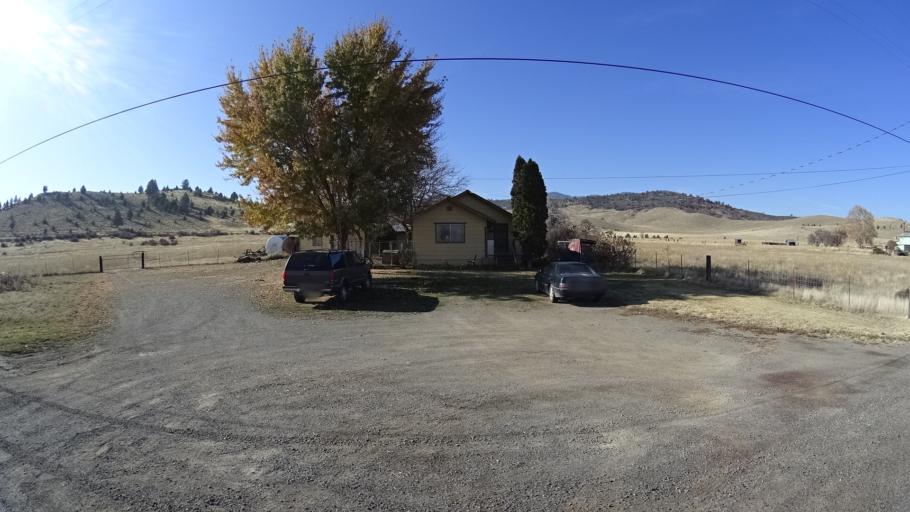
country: US
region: California
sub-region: Siskiyou County
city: Montague
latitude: 41.6445
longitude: -122.5366
